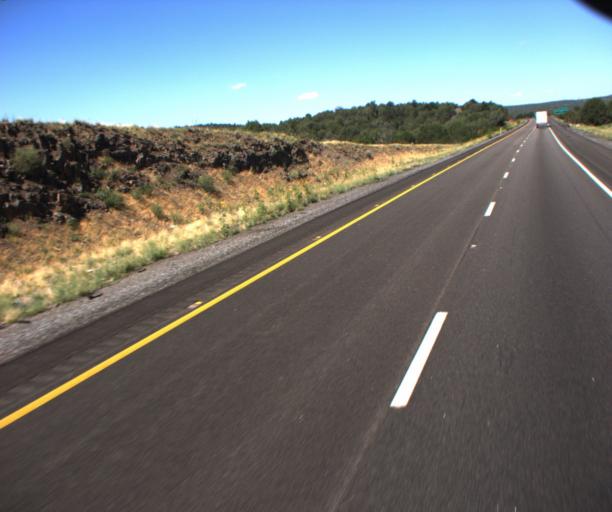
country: US
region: Arizona
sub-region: Mohave County
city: Peach Springs
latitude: 35.2090
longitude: -113.2747
